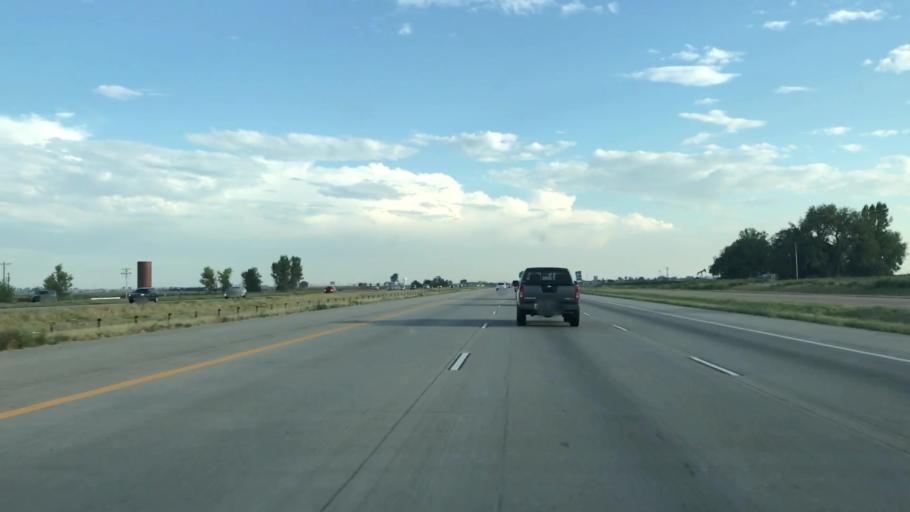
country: US
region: Colorado
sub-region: Weld County
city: Frederick
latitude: 40.1040
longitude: -104.9809
